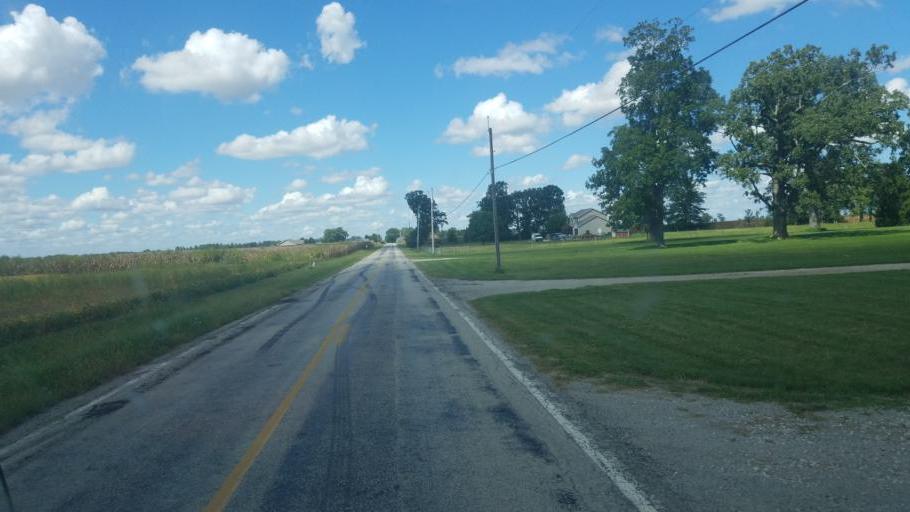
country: US
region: Ohio
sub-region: Madison County
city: West Jefferson
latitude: 40.0072
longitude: -83.3580
